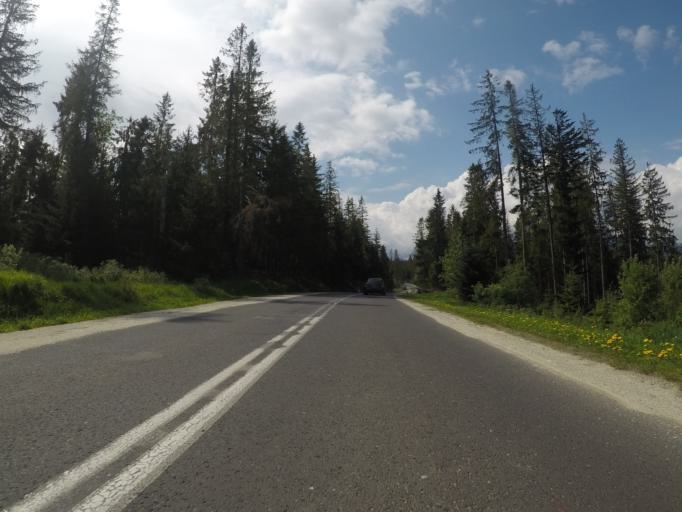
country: PL
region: Lesser Poland Voivodeship
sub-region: Powiat tatrzanski
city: Bukowina Tatrzanska
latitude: 49.2918
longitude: 20.1140
